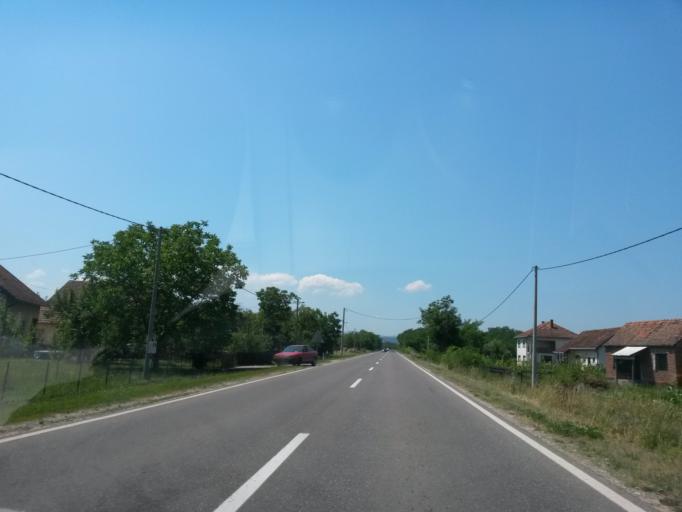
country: BA
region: Federation of Bosnia and Herzegovina
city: Odzak
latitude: 44.9747
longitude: 18.3547
